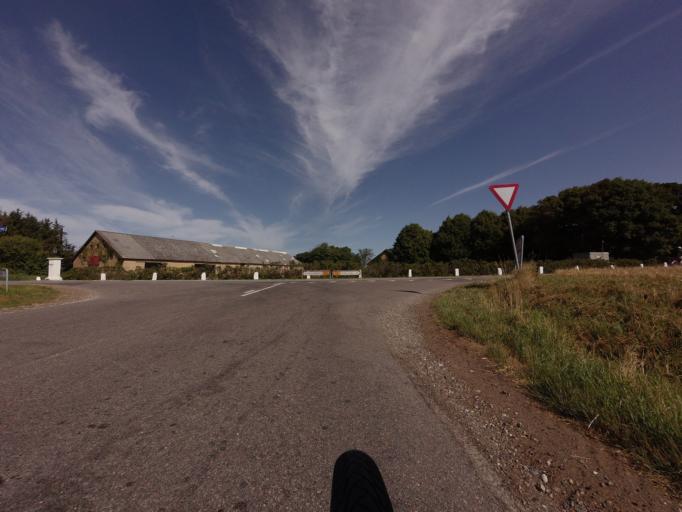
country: DK
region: North Denmark
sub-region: Hjorring Kommune
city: Vra
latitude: 57.4145
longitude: 9.8909
